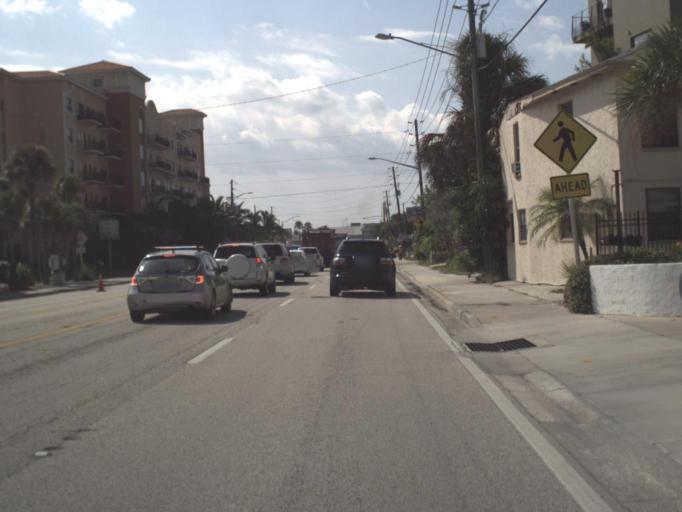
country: US
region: Florida
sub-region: Pinellas County
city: Madeira Beach
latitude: 27.7898
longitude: -82.7875
